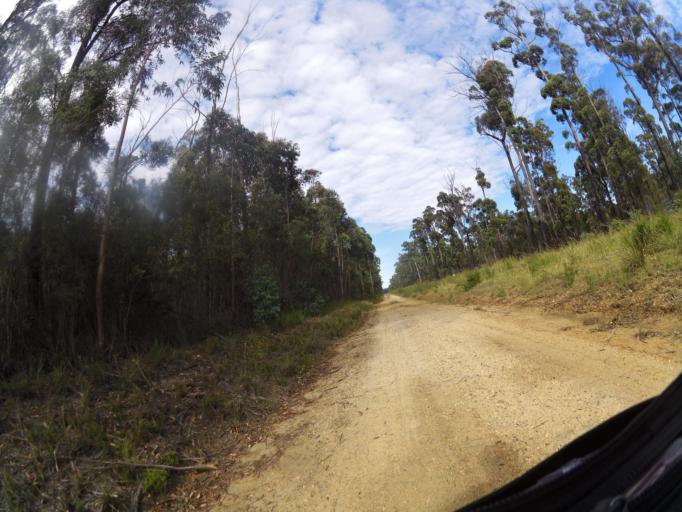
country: AU
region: Victoria
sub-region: East Gippsland
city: Lakes Entrance
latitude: -37.7457
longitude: 148.2401
